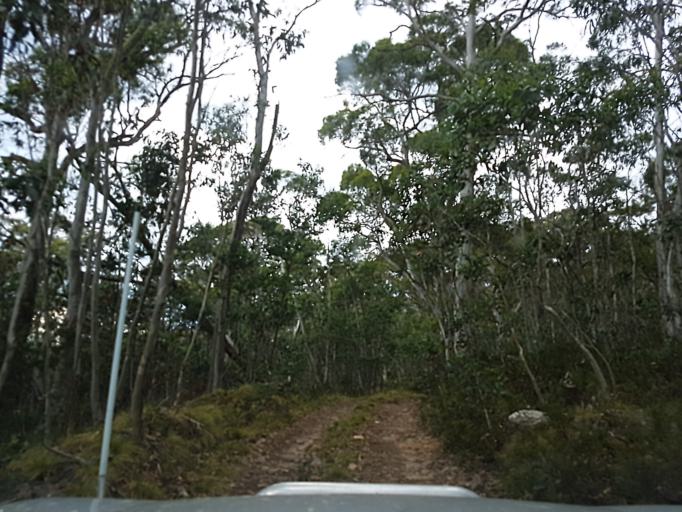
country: AU
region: New South Wales
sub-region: Snowy River
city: Jindabyne
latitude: -36.8815
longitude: 148.1583
